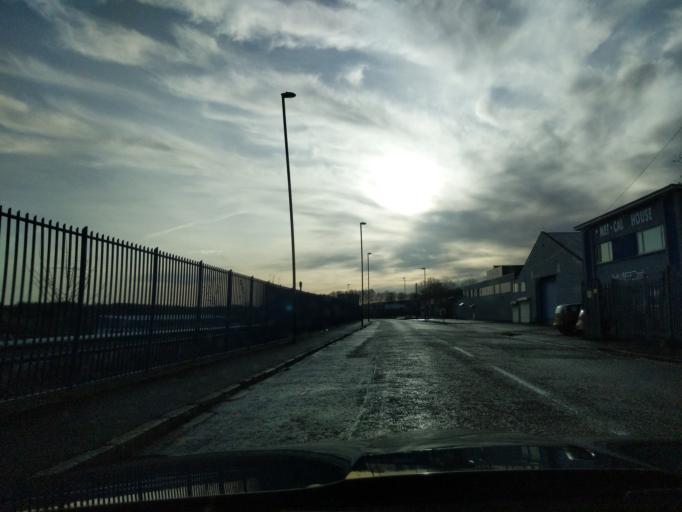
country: GB
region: England
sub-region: Borough of North Tyneside
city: Wallsend
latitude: 54.9813
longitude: -1.5376
